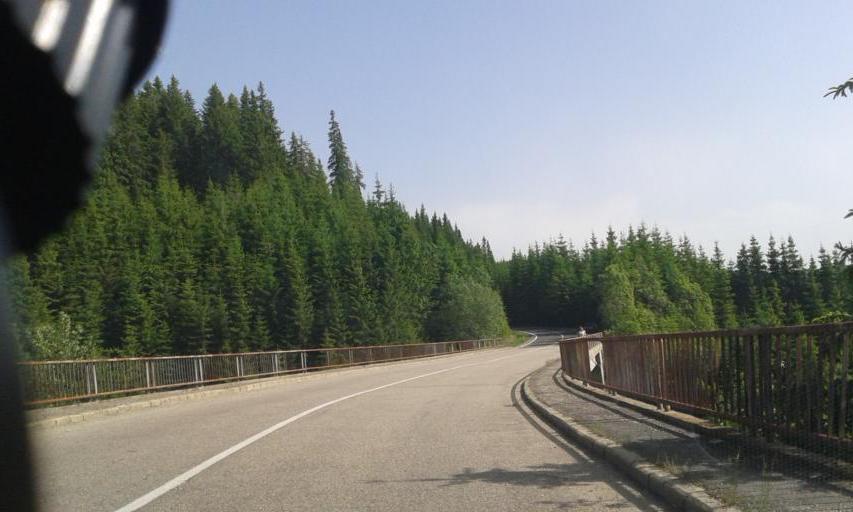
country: RO
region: Alba
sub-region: Comuna Sugag
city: Sugag
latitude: 45.5592
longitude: 23.6194
